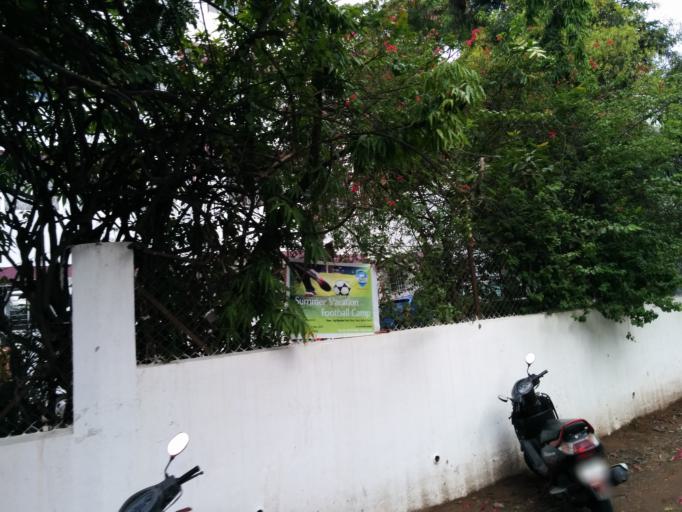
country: IN
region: Maharashtra
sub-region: Pune Division
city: Pune
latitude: 18.5117
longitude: 73.8155
